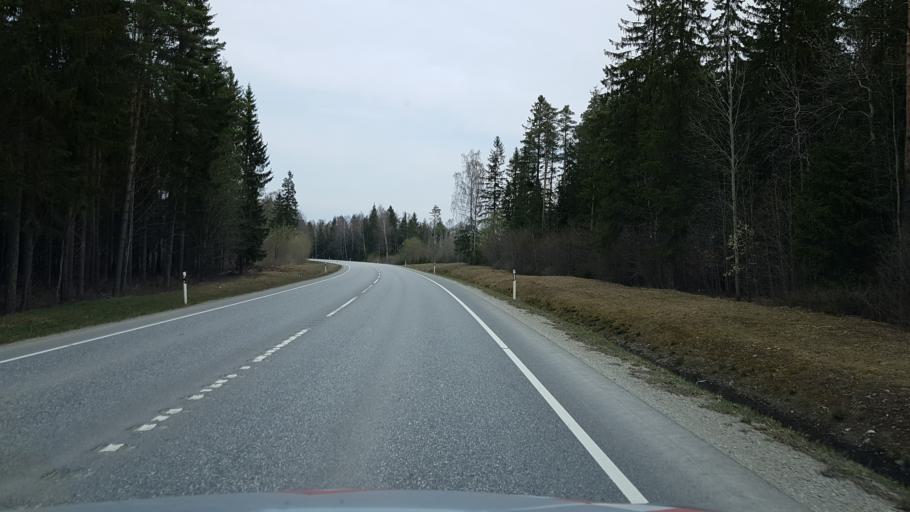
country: EE
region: Laeaene-Virumaa
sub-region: Someru vald
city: Someru
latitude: 59.3387
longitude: 26.4116
